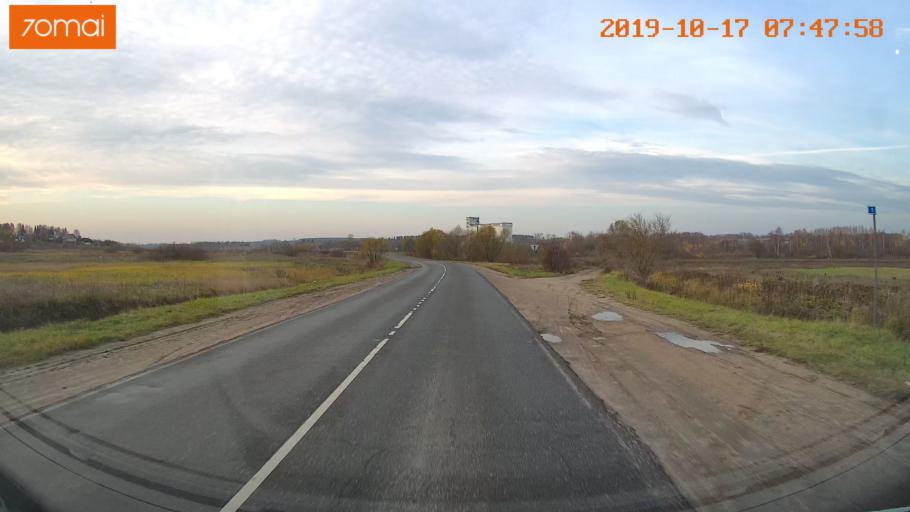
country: RU
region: Vladimir
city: Yur'yev-Pol'skiy
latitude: 56.4844
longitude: 39.6790
